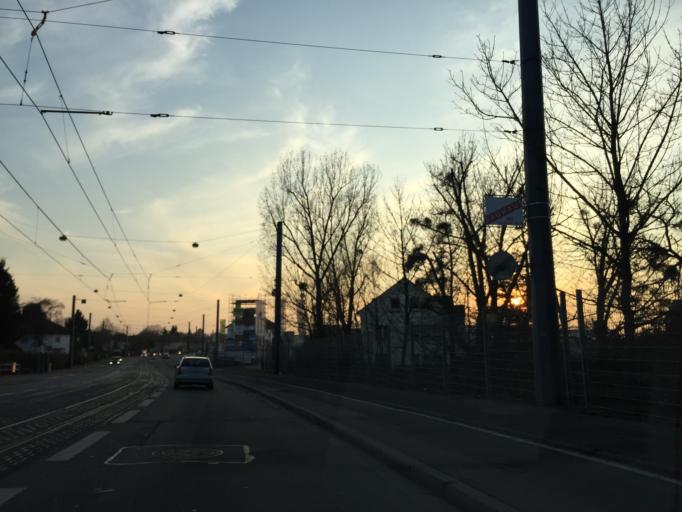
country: DE
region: Baden-Wuerttemberg
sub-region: Karlsruhe Region
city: Eppelheim
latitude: 49.4052
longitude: 8.6505
